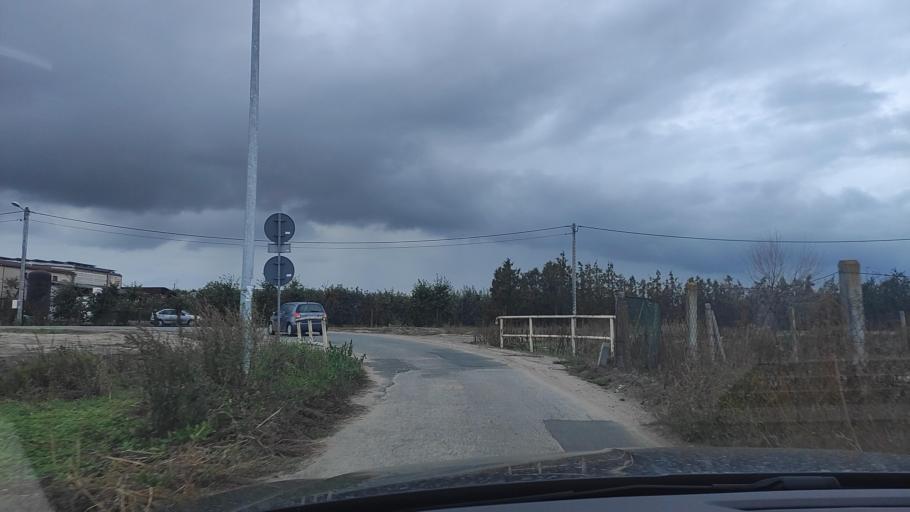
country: PL
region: Greater Poland Voivodeship
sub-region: Powiat poznanski
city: Kostrzyn
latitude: 52.3980
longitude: 17.1784
